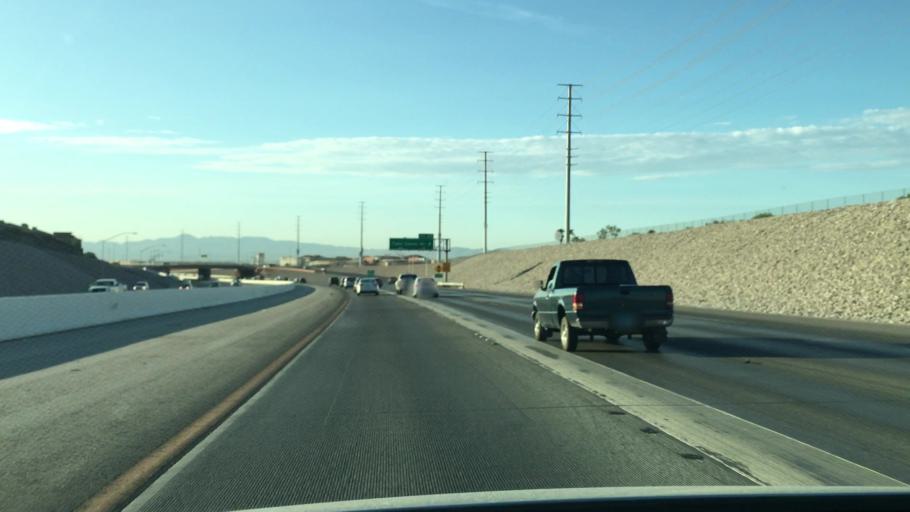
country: US
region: Nevada
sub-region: Clark County
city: Summerlin South
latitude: 36.1254
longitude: -115.3320
